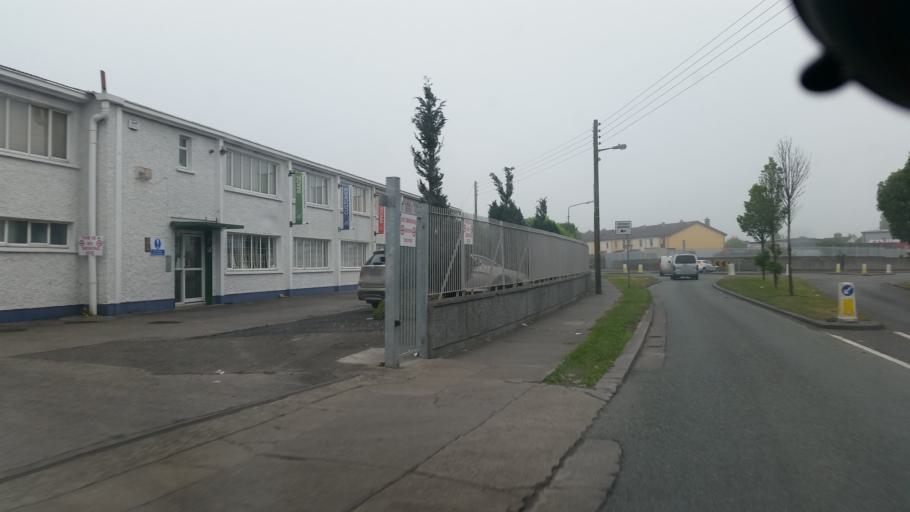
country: IE
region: Leinster
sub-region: Dublin City
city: Finglas
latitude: 53.3980
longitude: -6.3041
